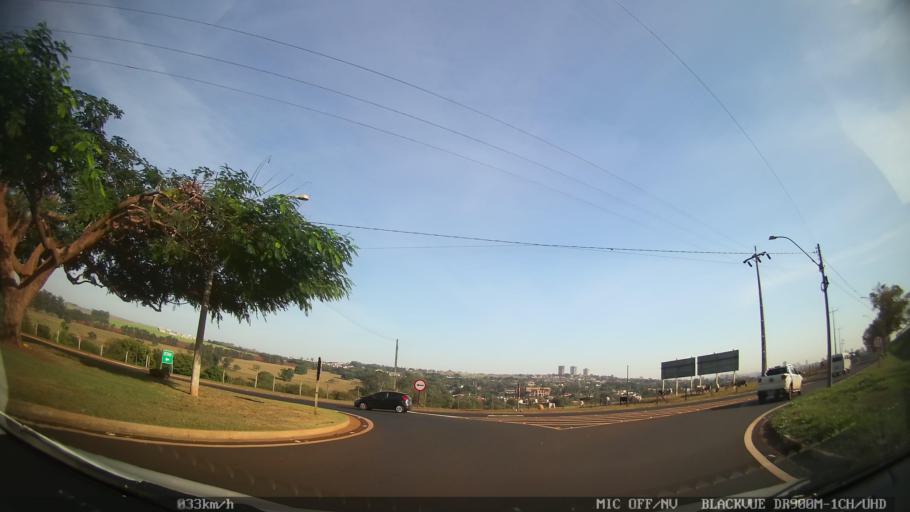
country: BR
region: Sao Paulo
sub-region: Ribeirao Preto
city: Ribeirao Preto
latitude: -21.2553
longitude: -47.8192
